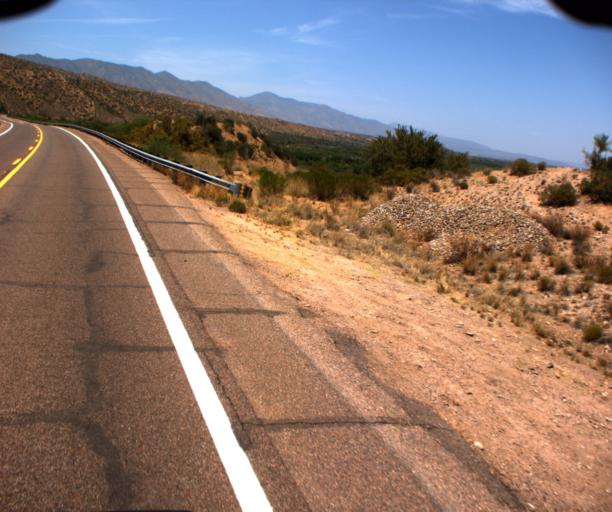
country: US
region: Arizona
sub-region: Gila County
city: Tonto Basin
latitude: 33.7552
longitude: -111.2459
